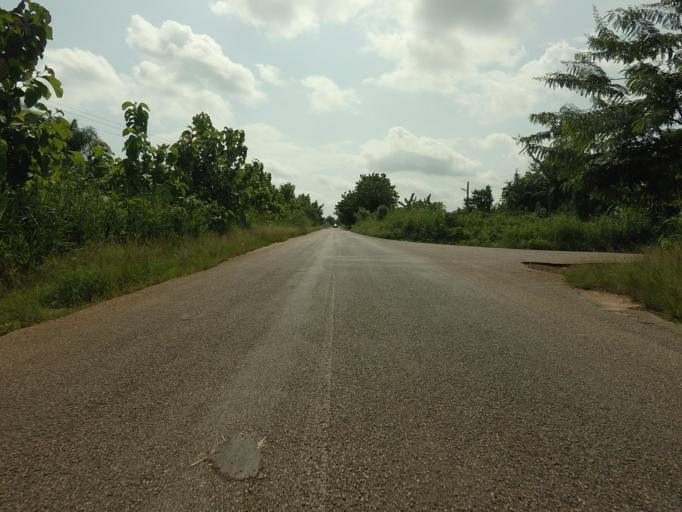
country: TG
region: Maritime
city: Lome
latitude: 6.2635
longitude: 0.9552
